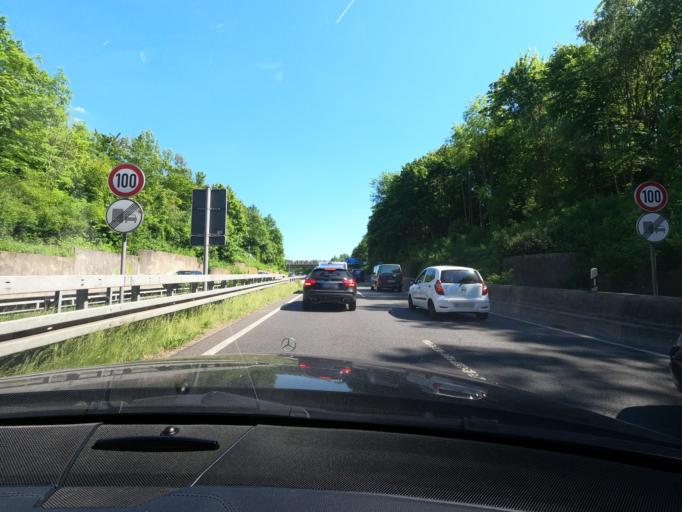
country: DE
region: North Rhine-Westphalia
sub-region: Regierungsbezirk Arnsberg
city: Bochum
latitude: 51.4558
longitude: 7.2010
